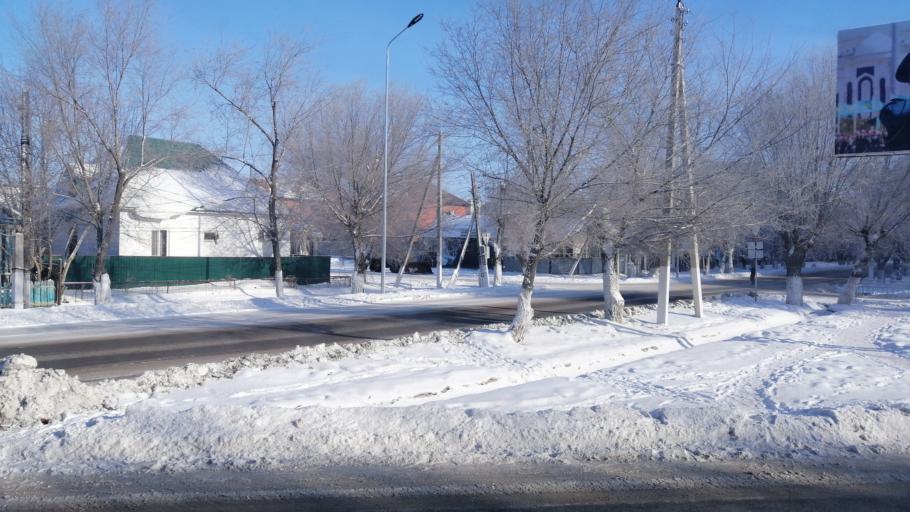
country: KZ
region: Aqtoebe
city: Aqtobe
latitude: 50.2854
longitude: 57.2119
